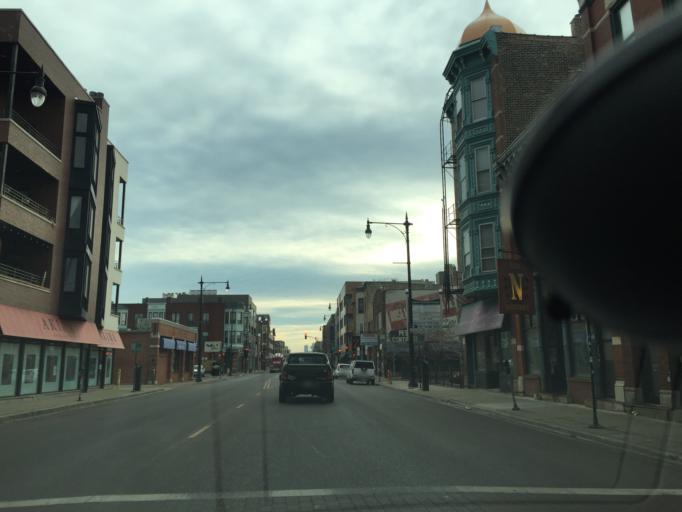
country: US
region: Illinois
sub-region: Cook County
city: Chicago
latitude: 41.9106
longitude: -87.6738
